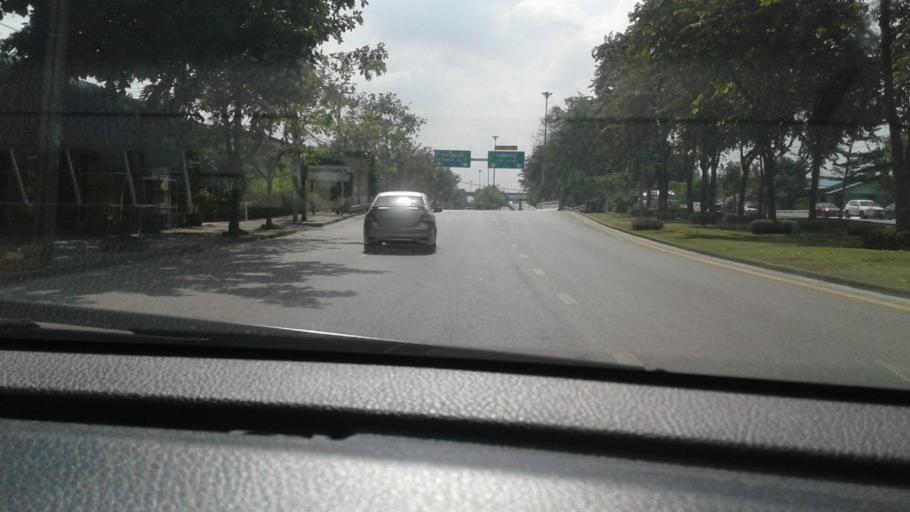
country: TH
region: Bangkok
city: Thawi Watthana
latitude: 13.7901
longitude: 100.3947
